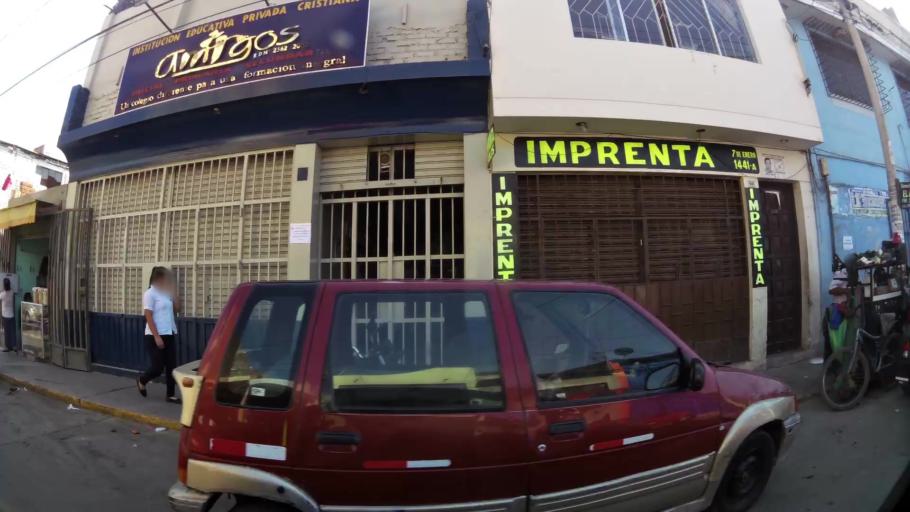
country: PE
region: Lambayeque
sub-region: Provincia de Chiclayo
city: Santa Rosa
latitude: -6.7664
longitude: -79.8368
